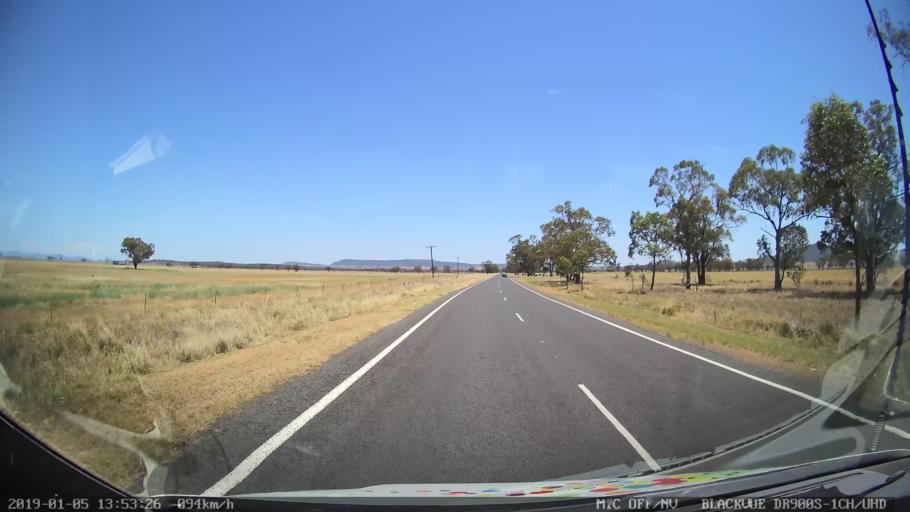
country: AU
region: New South Wales
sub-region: Gunnedah
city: Gunnedah
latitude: -31.0751
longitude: 150.2773
